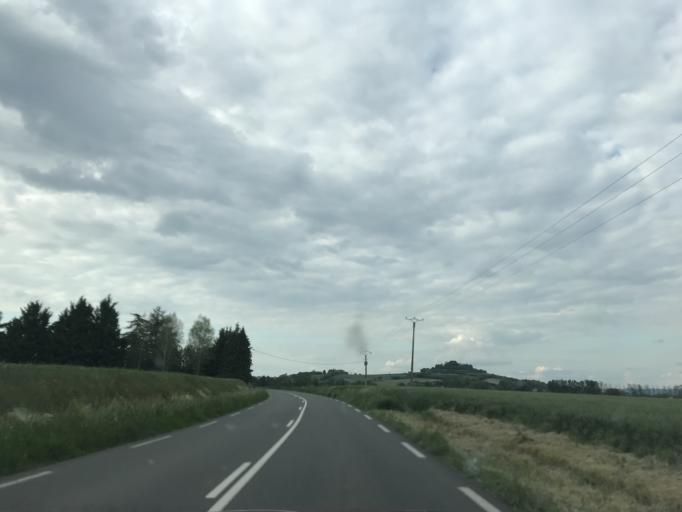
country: FR
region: Auvergne
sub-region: Departement du Puy-de-Dome
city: Maringues
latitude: 45.9337
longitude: 3.3410
